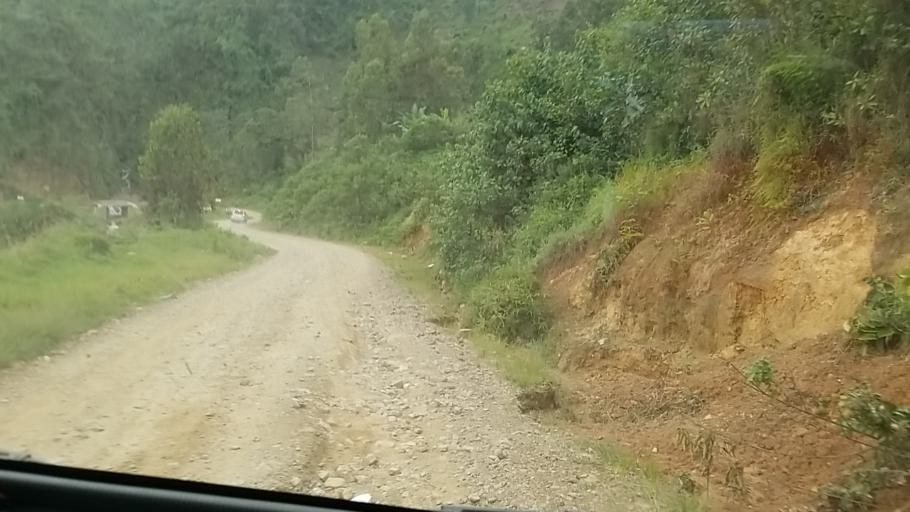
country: CD
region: Nord Kivu
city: Sake
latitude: -1.9644
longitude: 28.9155
